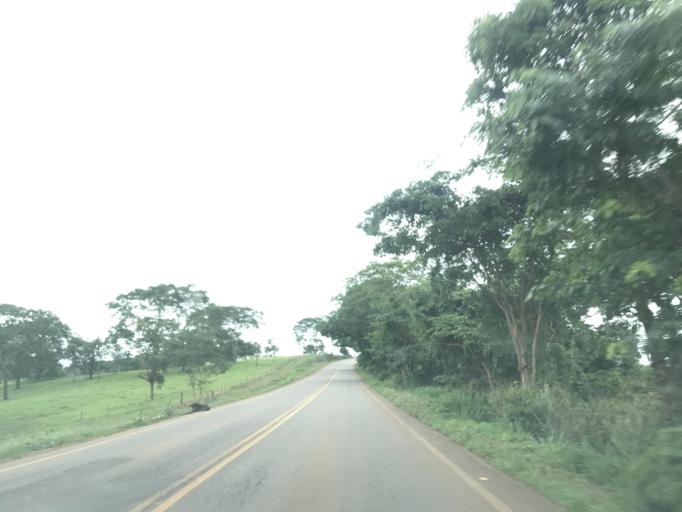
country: BR
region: Goias
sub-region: Vianopolis
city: Vianopolis
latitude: -16.7112
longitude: -48.4011
